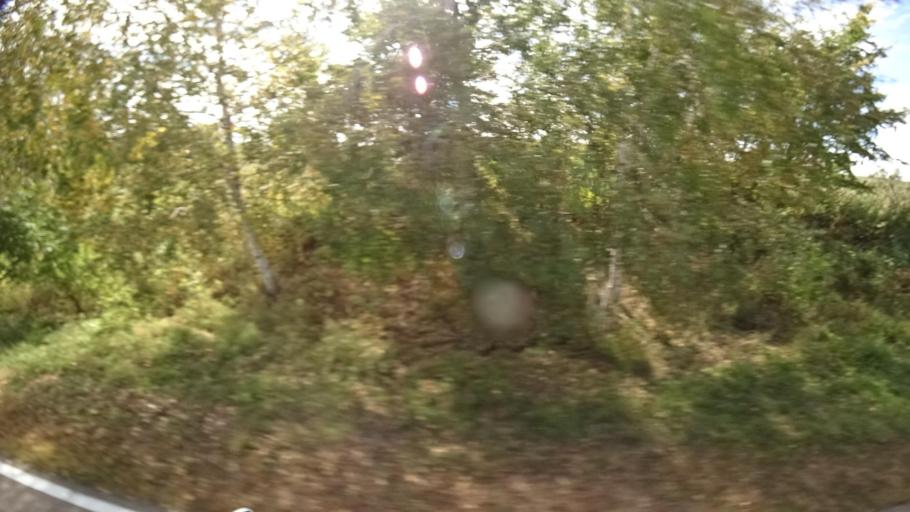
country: RU
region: Primorskiy
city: Yakovlevka
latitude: 44.4109
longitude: 133.5881
